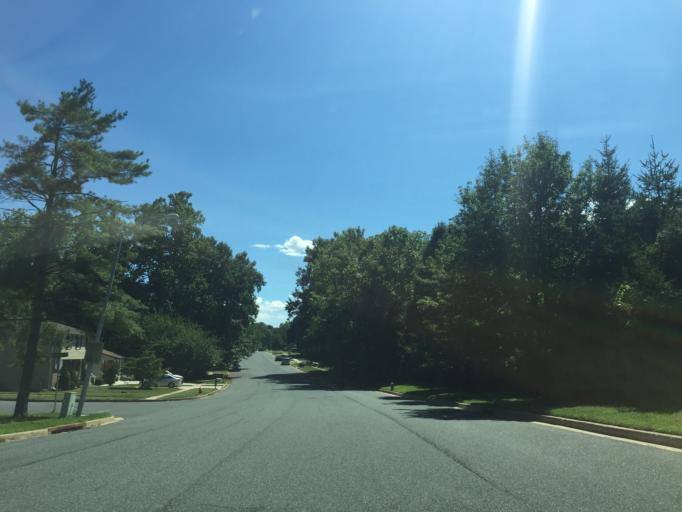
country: US
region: Maryland
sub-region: Baltimore County
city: Perry Hall
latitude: 39.4148
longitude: -76.4772
